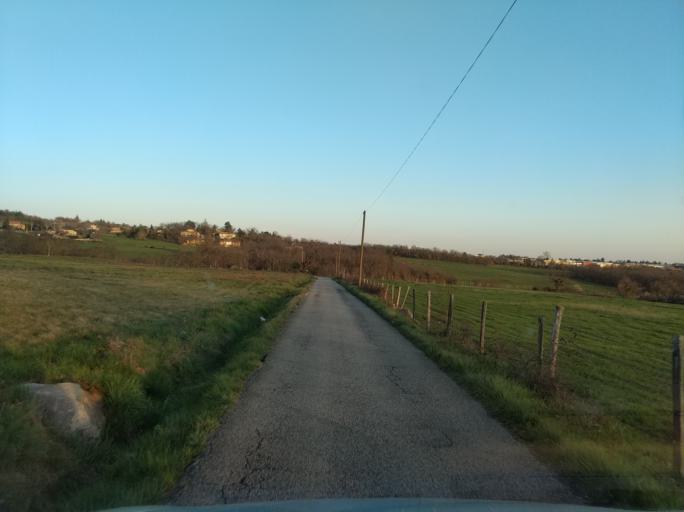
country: FR
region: Rhone-Alpes
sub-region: Departement de l'Ardeche
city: Boulieu-les-Annonay
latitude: 45.2677
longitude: 4.6854
